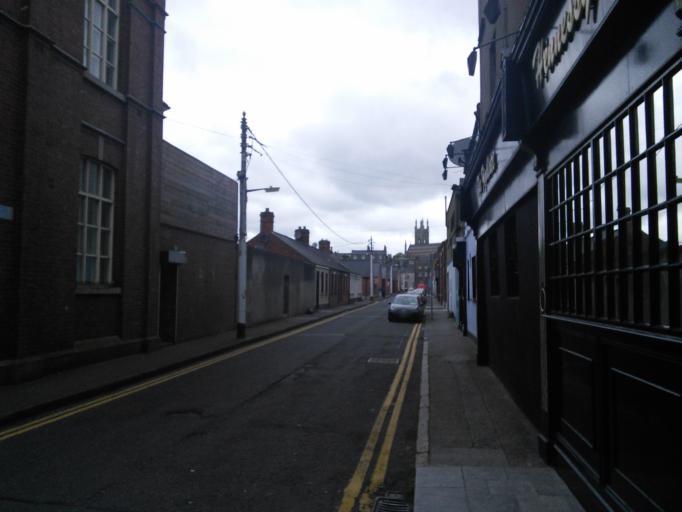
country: IE
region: Leinster
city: Drumcondra
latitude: 53.3570
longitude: -6.2645
